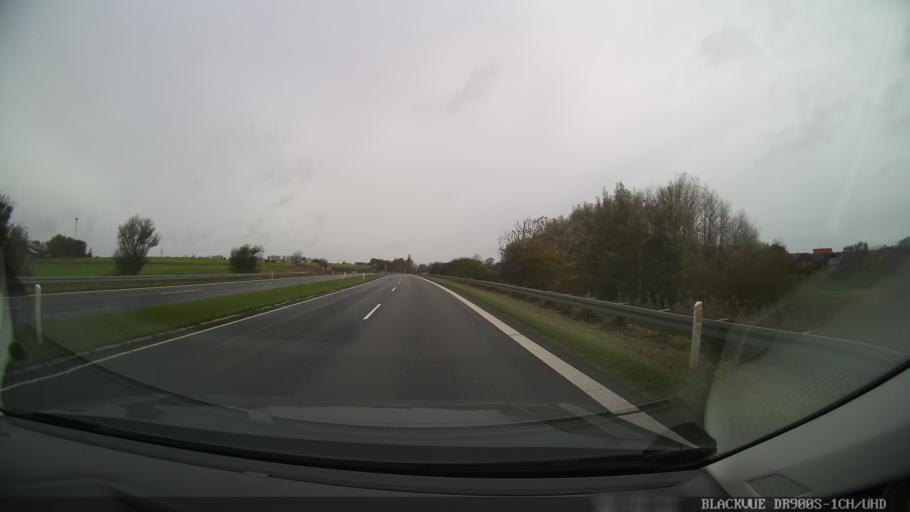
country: DK
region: North Denmark
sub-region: Thisted Kommune
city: Thisted
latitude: 56.8729
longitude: 8.6711
